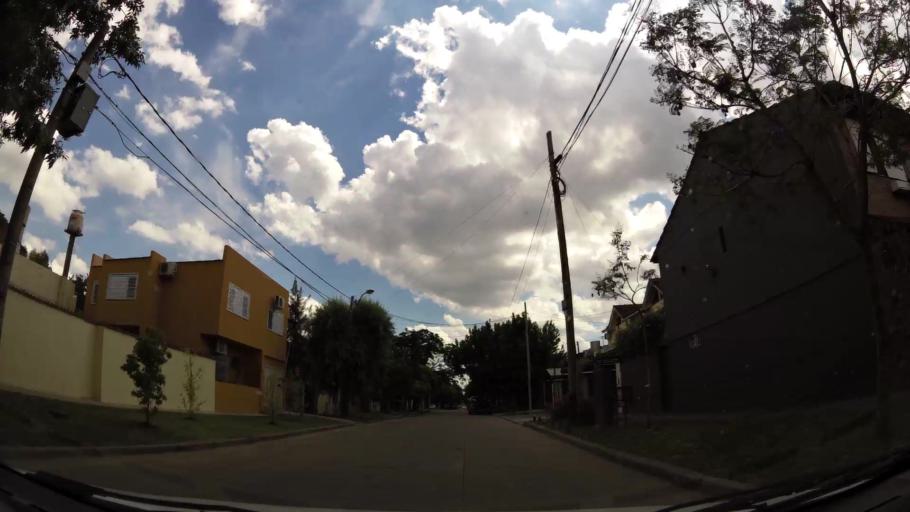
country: AR
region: Buenos Aires
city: Ituzaingo
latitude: -34.6481
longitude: -58.6686
